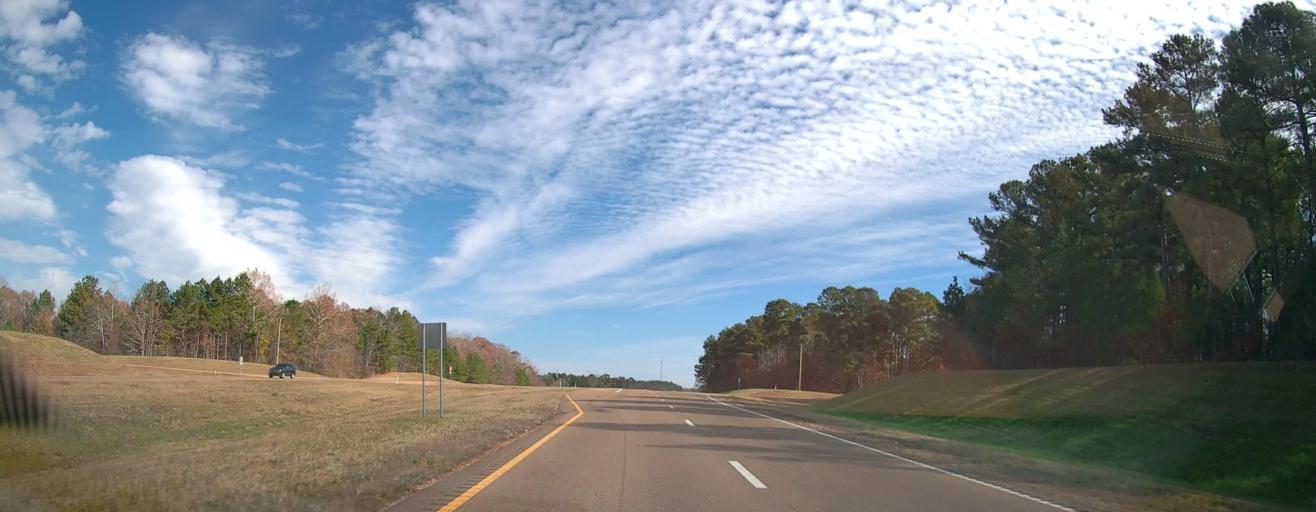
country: US
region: Mississippi
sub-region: Benton County
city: Ashland
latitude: 34.9539
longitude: -89.0344
